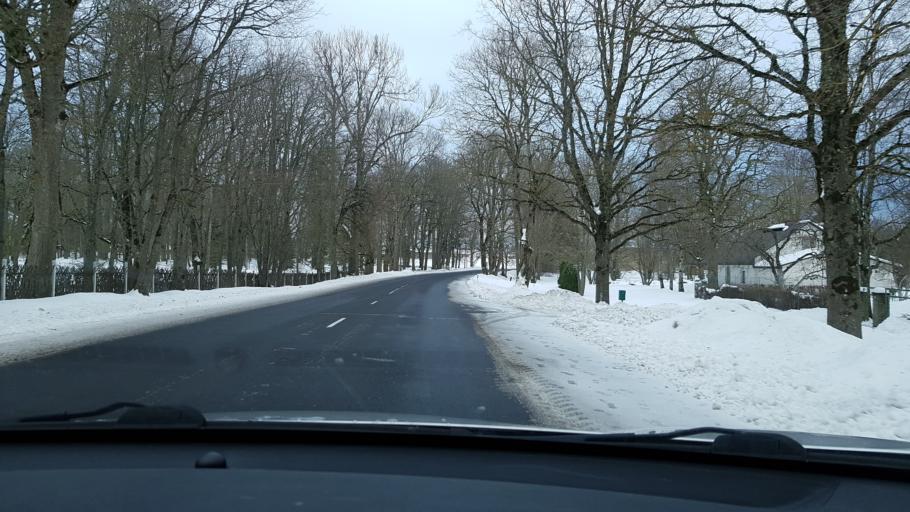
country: EE
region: Jaervamaa
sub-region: Paide linn
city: Paide
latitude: 58.8923
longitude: 25.7134
